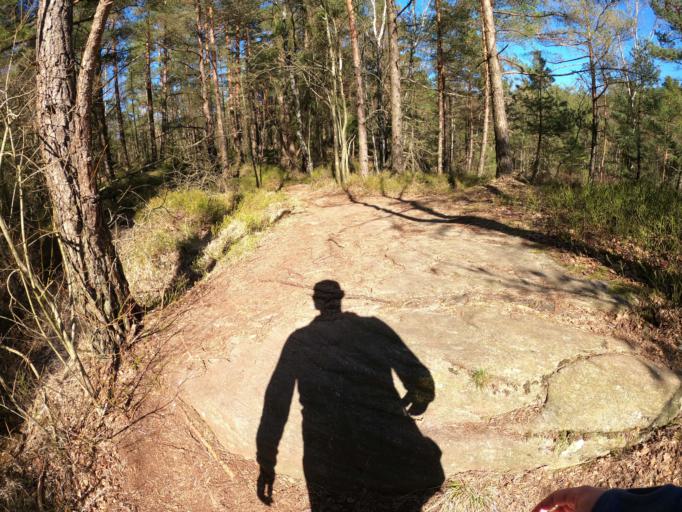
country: SE
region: Vaestra Goetaland
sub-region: Harryda Kommun
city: Molnlycke
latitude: 57.6410
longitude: 12.1157
